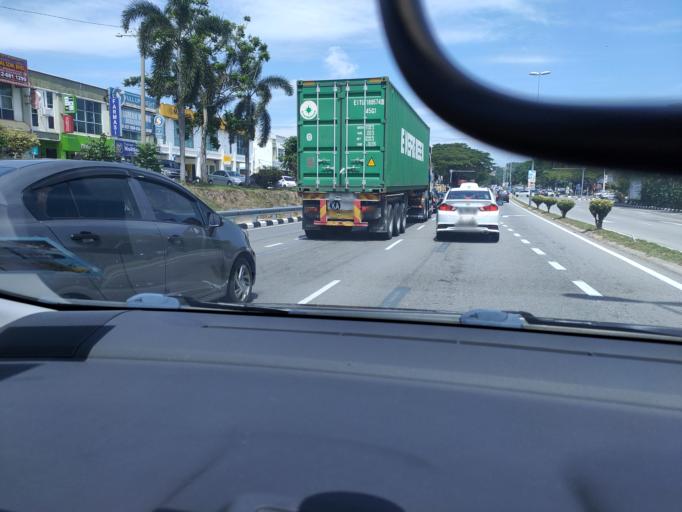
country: MY
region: Melaka
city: Bukit Rambai
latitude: 2.2710
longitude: 102.2167
